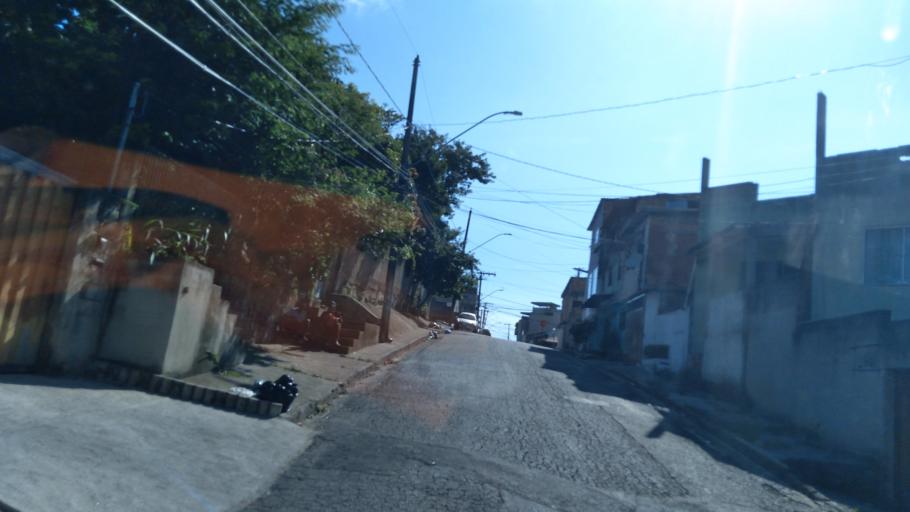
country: BR
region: Minas Gerais
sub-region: Belo Horizonte
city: Belo Horizonte
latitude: -19.9020
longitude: -43.8909
